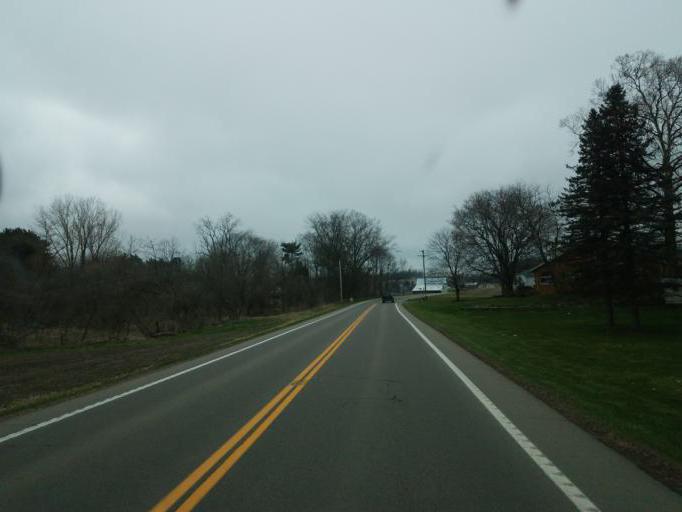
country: US
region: Ohio
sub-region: Ashland County
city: Loudonville
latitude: 40.6961
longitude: -82.2424
